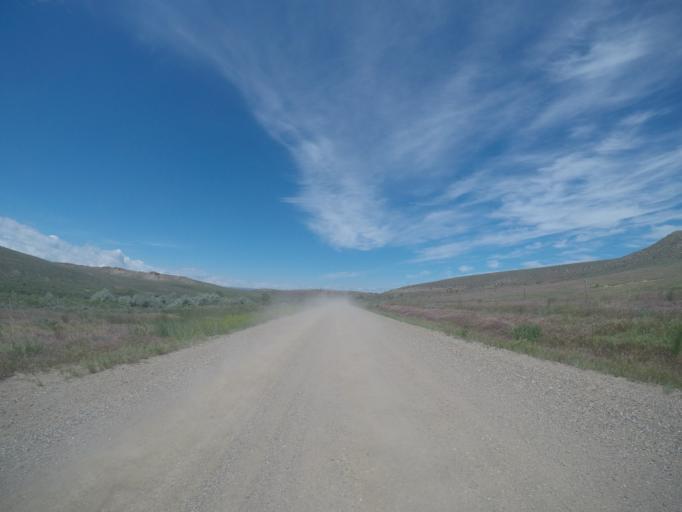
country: US
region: Montana
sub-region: Carbon County
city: Red Lodge
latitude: 45.2307
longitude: -108.8462
